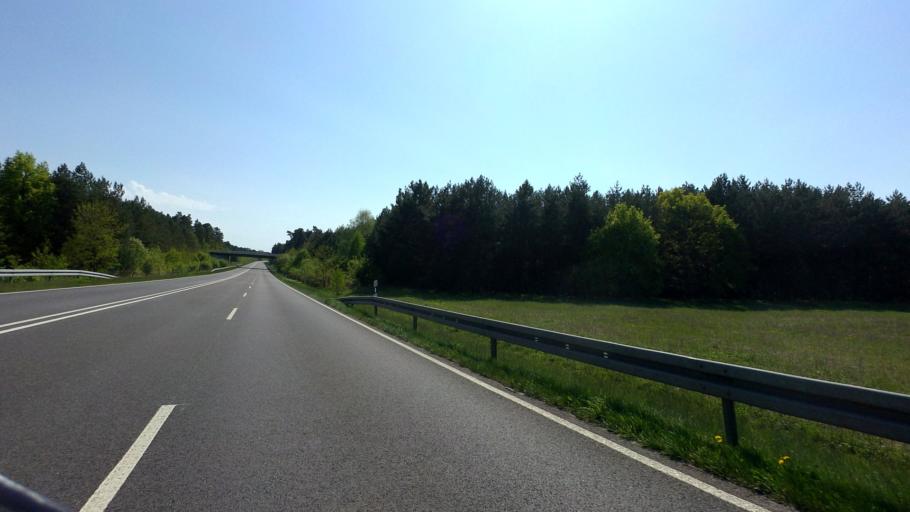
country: DE
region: Brandenburg
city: Beeskow
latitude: 52.1633
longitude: 14.2168
